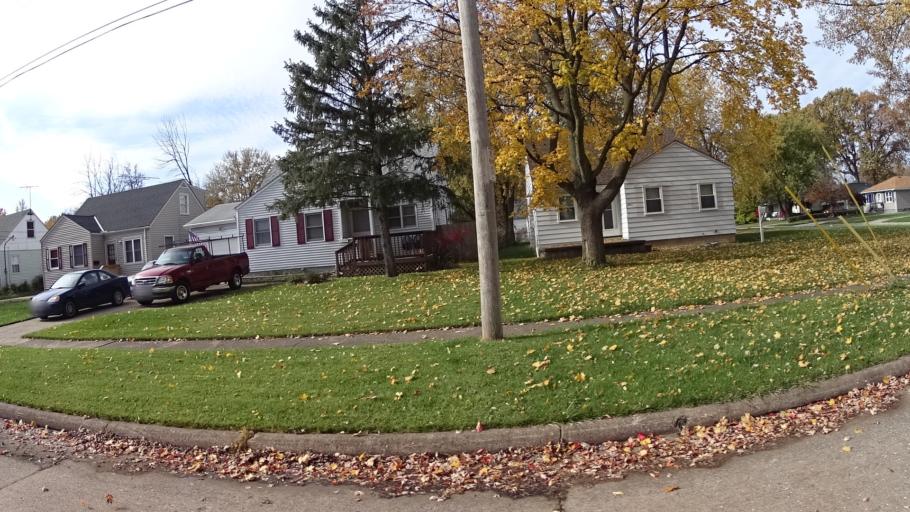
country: US
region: Ohio
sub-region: Lorain County
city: Sheffield Lake
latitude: 41.4720
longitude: -82.1351
